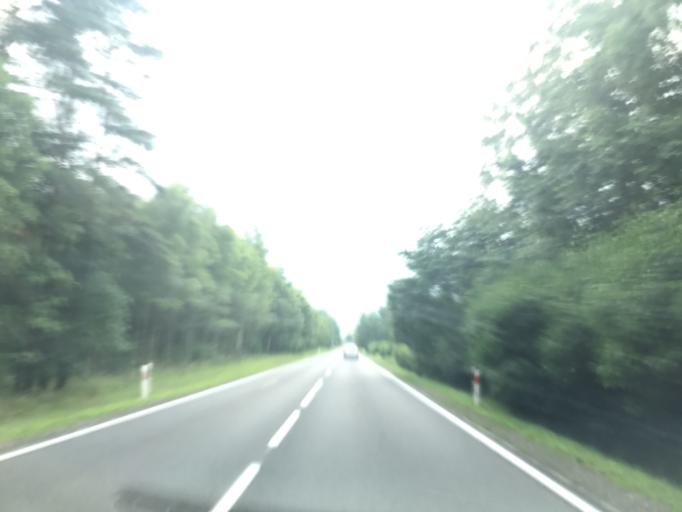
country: PL
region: Pomeranian Voivodeship
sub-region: Powiat czluchowski
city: Rzeczenica
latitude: 53.7505
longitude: 17.1524
